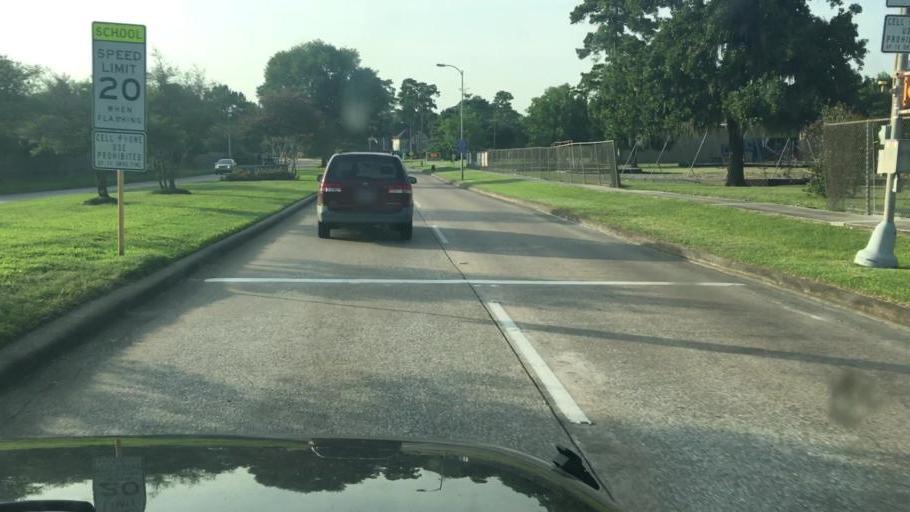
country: US
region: Texas
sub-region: Harris County
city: Atascocita
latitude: 30.0024
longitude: -95.1637
